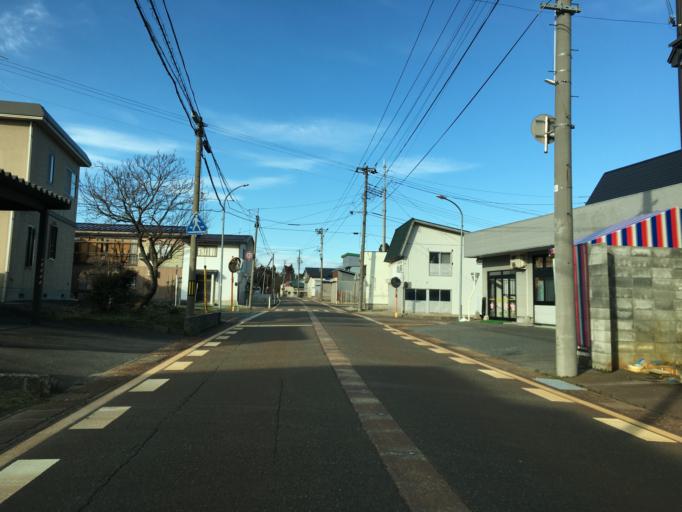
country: JP
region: Yamagata
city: Nagai
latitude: 38.0263
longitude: 139.9784
